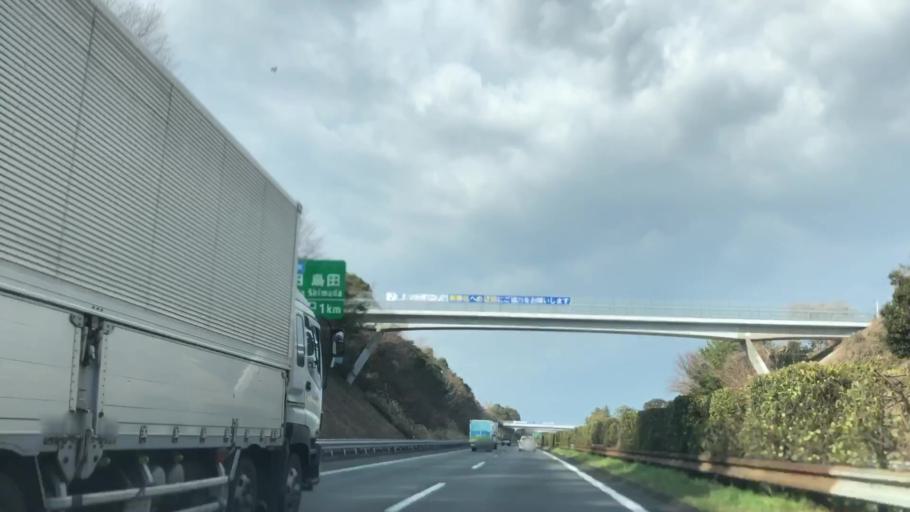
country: JP
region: Shizuoka
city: Shimada
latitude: 34.7805
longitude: 138.2295
